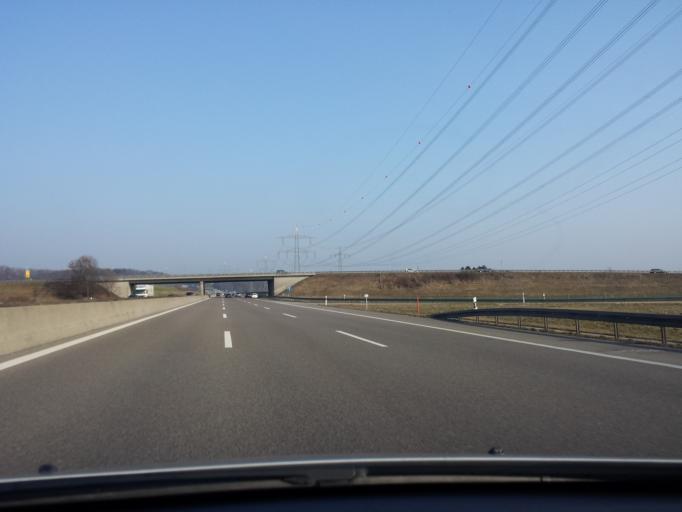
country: DE
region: Bavaria
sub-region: Swabia
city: Friedberg
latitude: 48.4045
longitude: 10.9520
